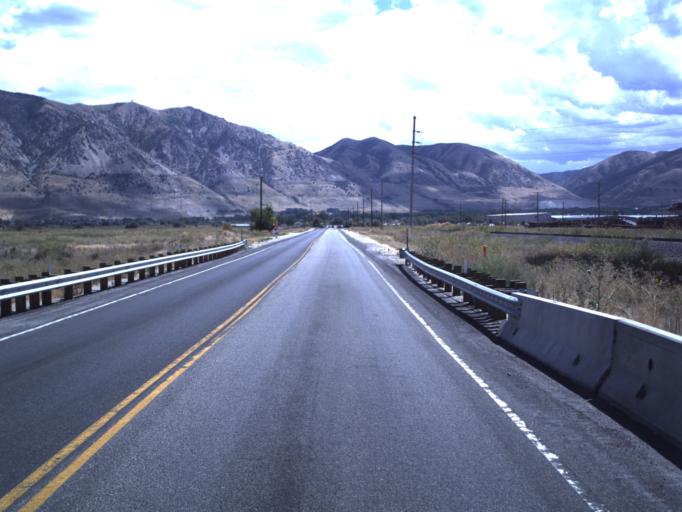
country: US
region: Utah
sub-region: Box Elder County
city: Brigham City
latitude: 41.5342
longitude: -112.0595
